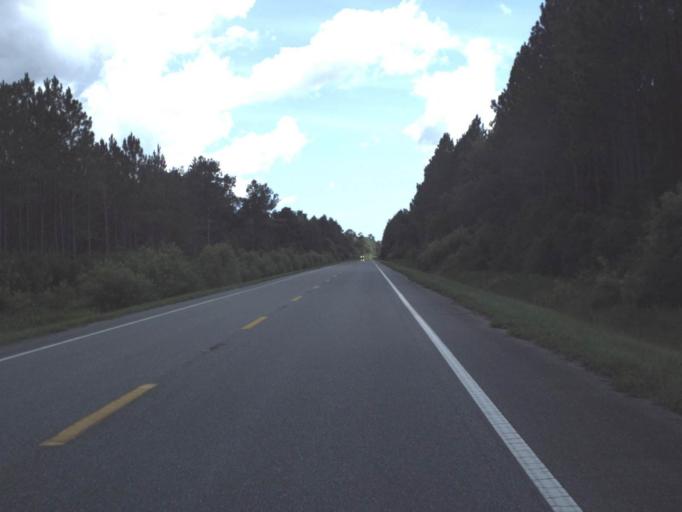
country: US
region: Florida
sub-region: Taylor County
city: Steinhatchee
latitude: 29.8628
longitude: -83.3084
